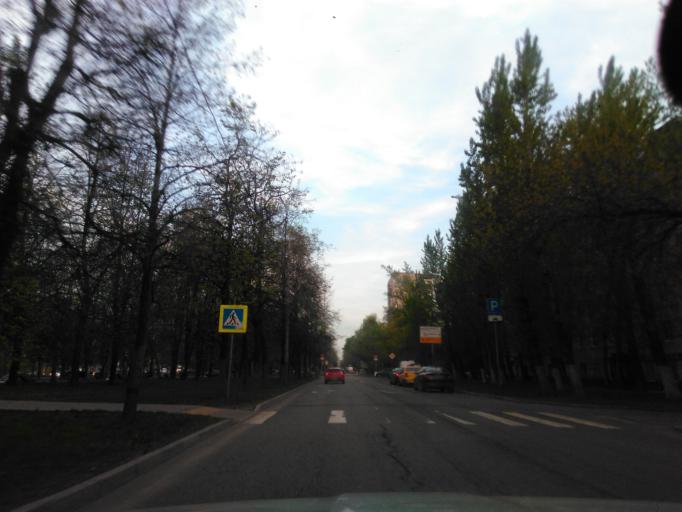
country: RU
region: Moscow
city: Novyye Kuz'minki
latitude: 55.7025
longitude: 37.7489
